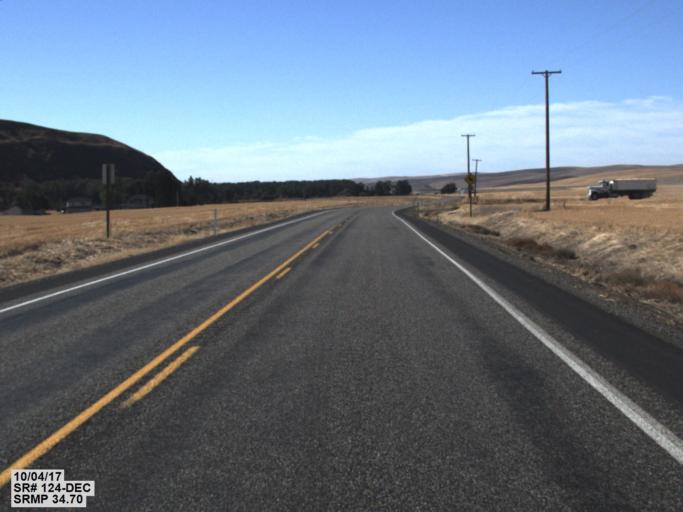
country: US
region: Washington
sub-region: Walla Walla County
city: Waitsburg
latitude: 46.2988
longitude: -118.3442
